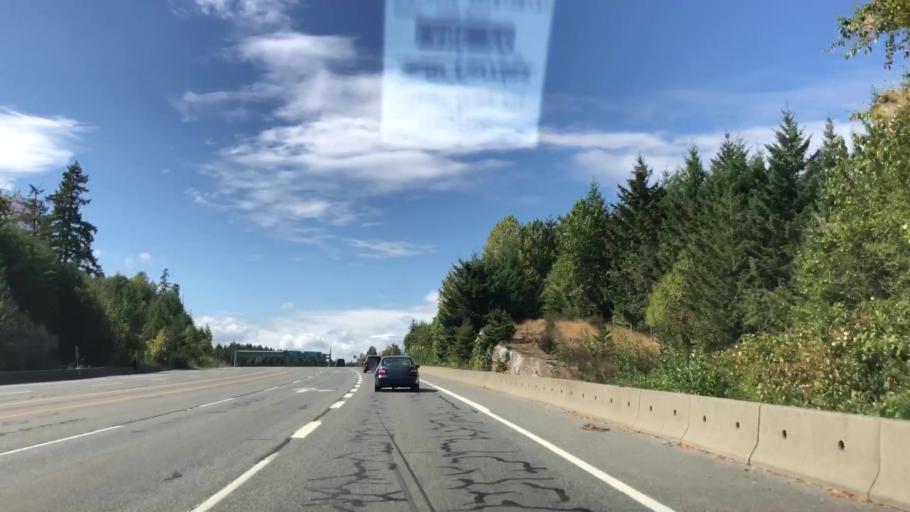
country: CA
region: British Columbia
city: Nanaimo
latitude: 49.1132
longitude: -123.8930
